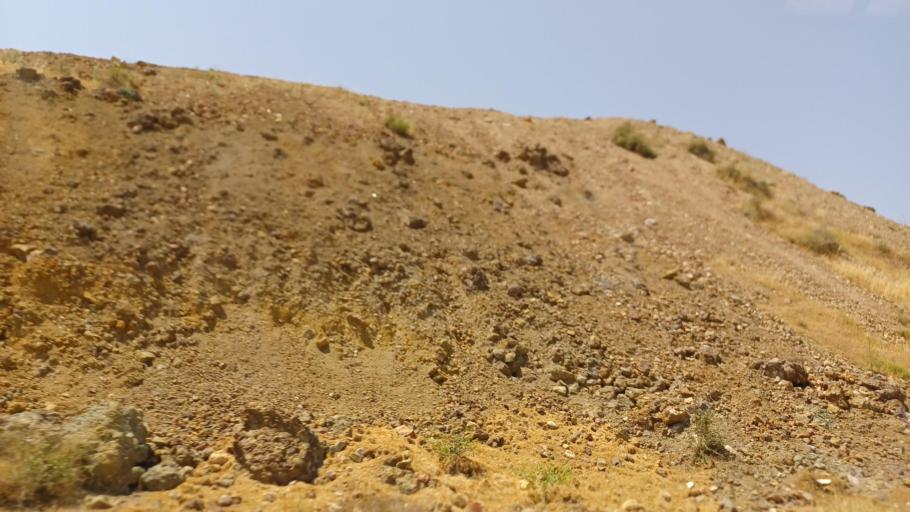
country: CY
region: Larnaka
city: Troulloi
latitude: 35.0322
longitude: 33.6232
